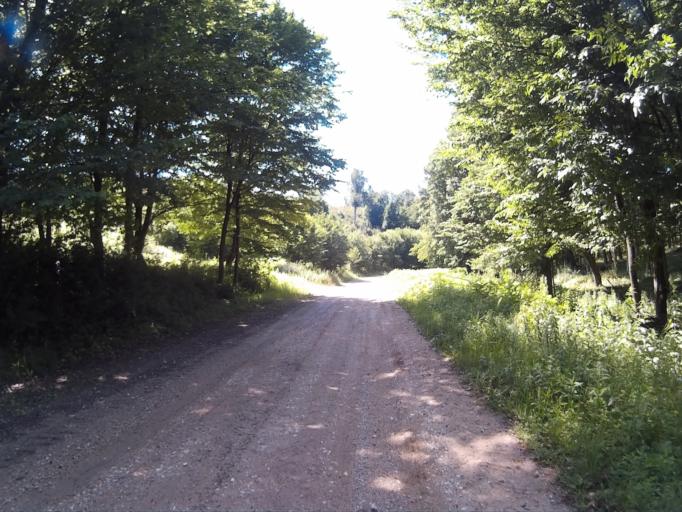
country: HU
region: Veszprem
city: Urkut
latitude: 47.1048
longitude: 17.6618
